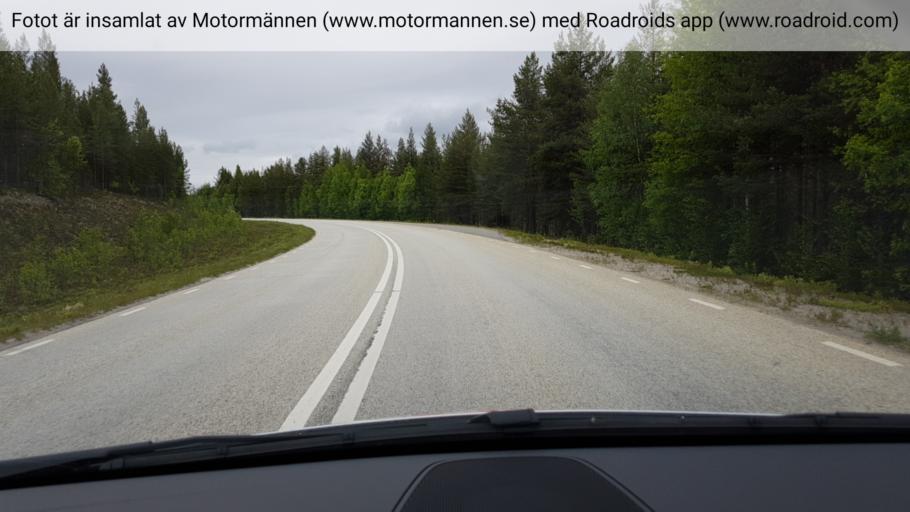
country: SE
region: Jaemtland
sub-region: Harjedalens Kommun
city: Sveg
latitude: 62.4168
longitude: 13.7699
